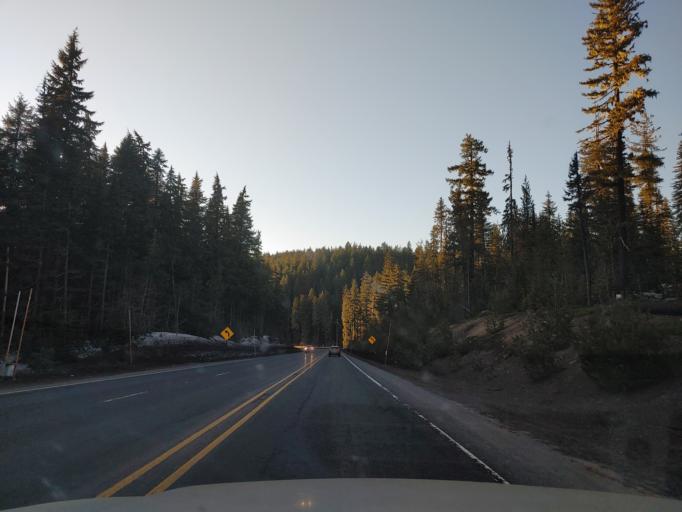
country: US
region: Oregon
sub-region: Lane County
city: Oakridge
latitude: 43.6096
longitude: -122.0581
